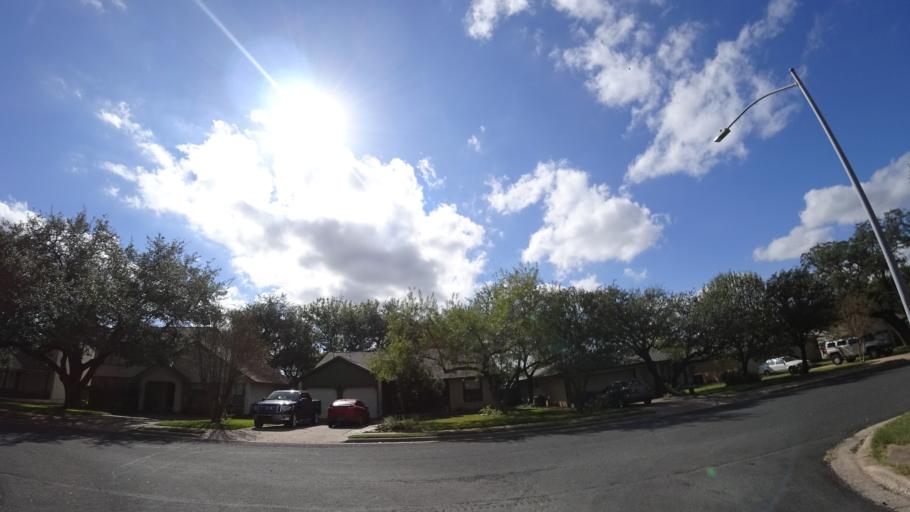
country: US
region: Texas
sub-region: Williamson County
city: Jollyville
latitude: 30.4225
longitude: -97.7285
